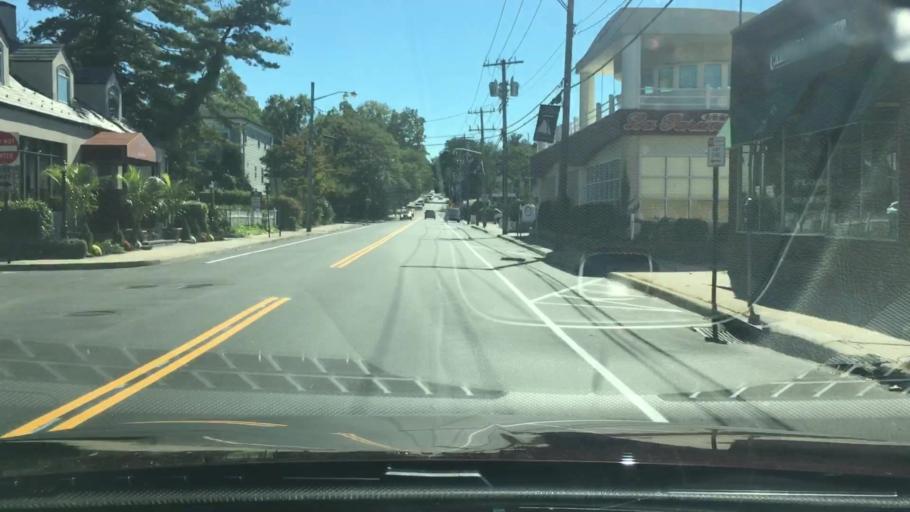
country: US
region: New York
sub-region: Nassau County
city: Port Washington
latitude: 40.8295
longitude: -73.7020
